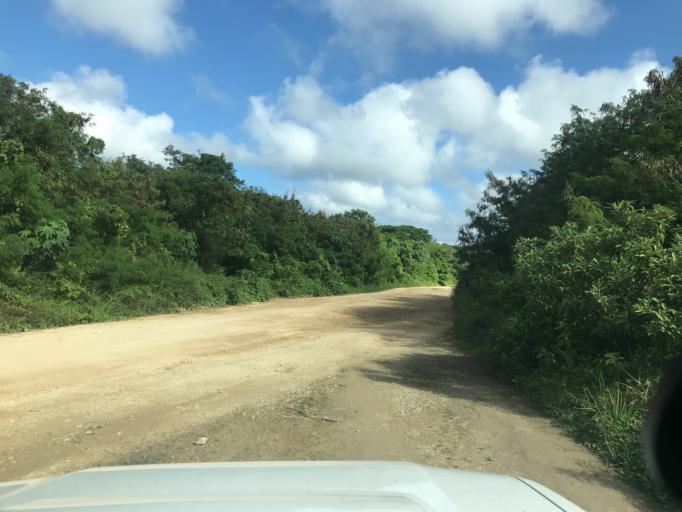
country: VU
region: Sanma
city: Luganville
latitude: -15.5102
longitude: 167.1255
